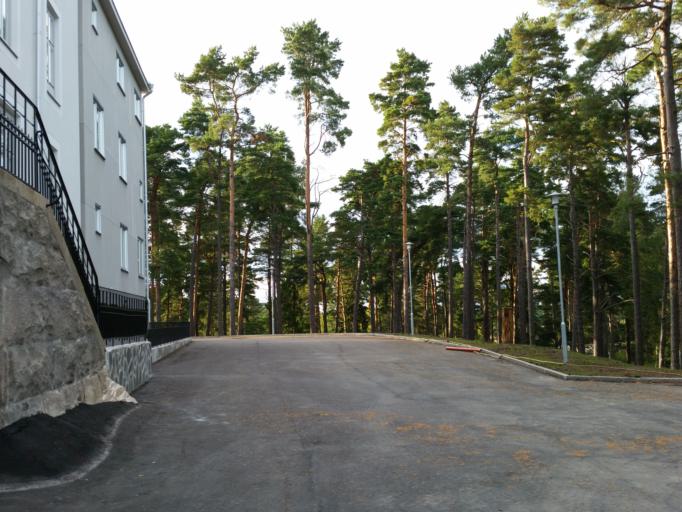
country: SE
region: Stockholm
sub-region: Upplands Vasby Kommun
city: Upplands Vaesby
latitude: 59.5415
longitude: 17.9144
